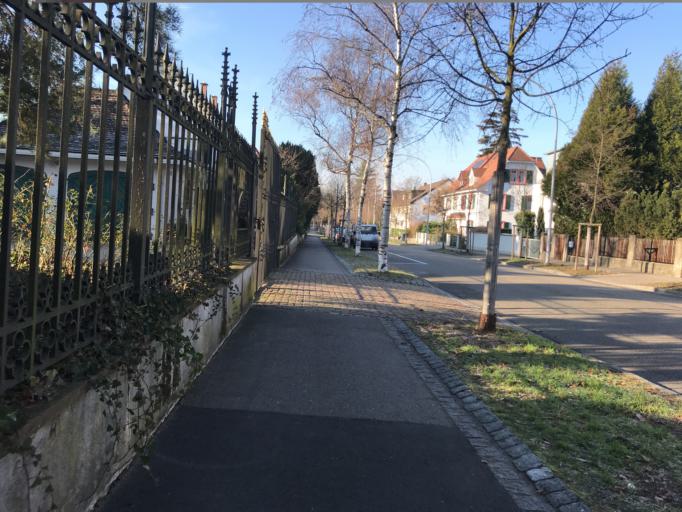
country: CH
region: Basel-City
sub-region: Basel-Stadt
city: Riehen
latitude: 47.5770
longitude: 7.6429
